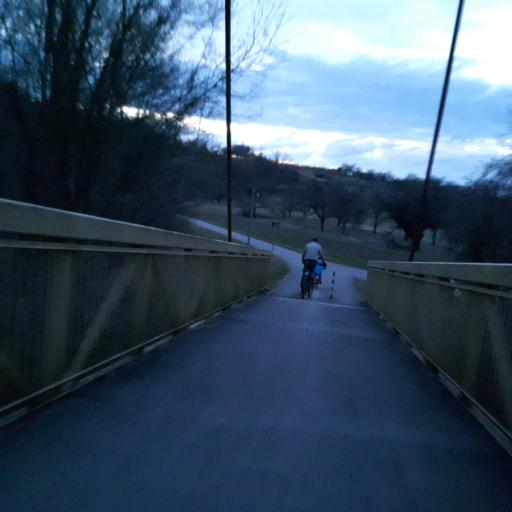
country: DE
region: Baden-Wuerttemberg
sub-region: Regierungsbezirk Stuttgart
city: Hessigheim
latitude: 48.9975
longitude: 9.1751
